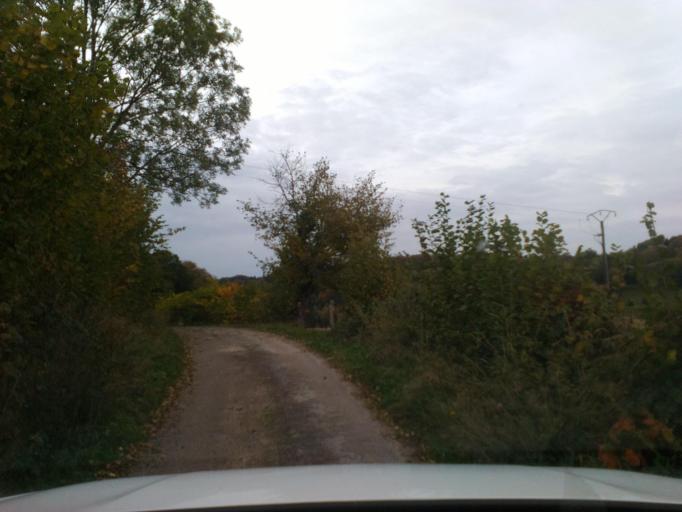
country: FR
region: Lorraine
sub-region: Departement des Vosges
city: Senones
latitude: 48.3328
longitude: 7.0137
